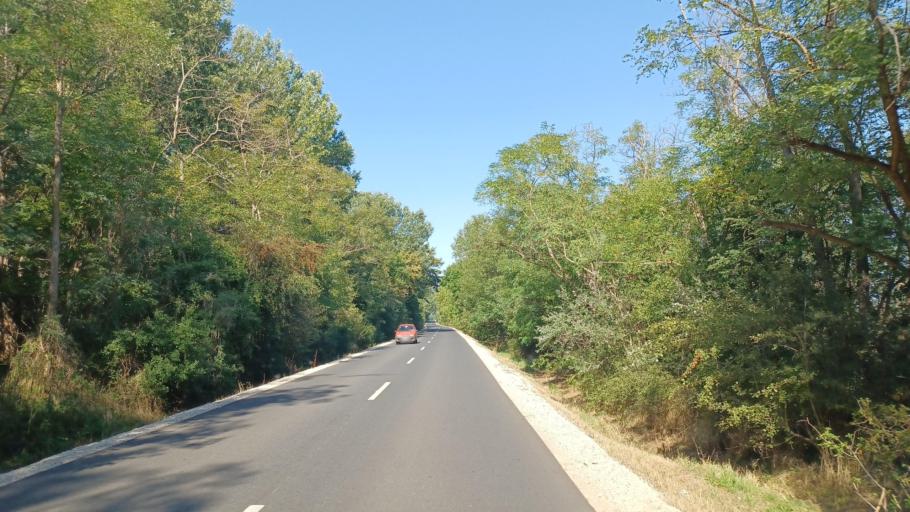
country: HU
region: Tolna
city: Nemetker
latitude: 46.7317
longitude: 18.7272
